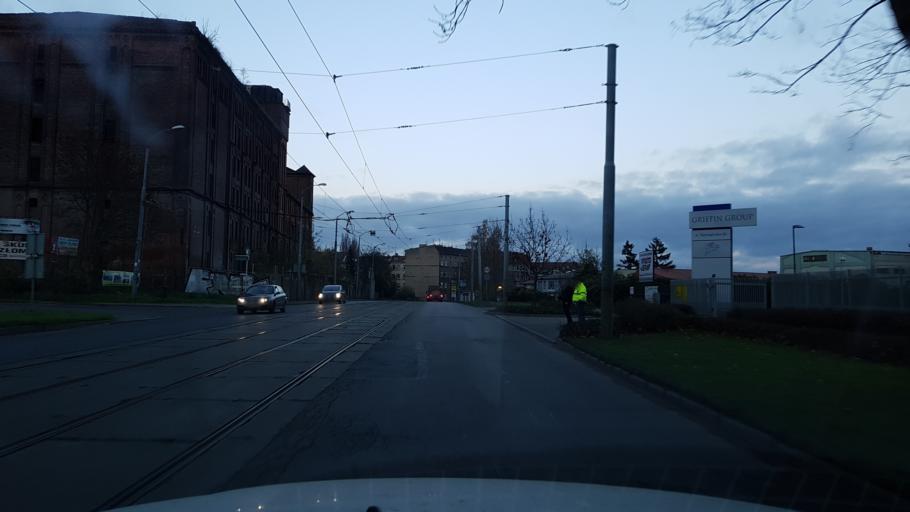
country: PL
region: West Pomeranian Voivodeship
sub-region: Szczecin
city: Szczecin
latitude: 53.4583
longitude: 14.5890
